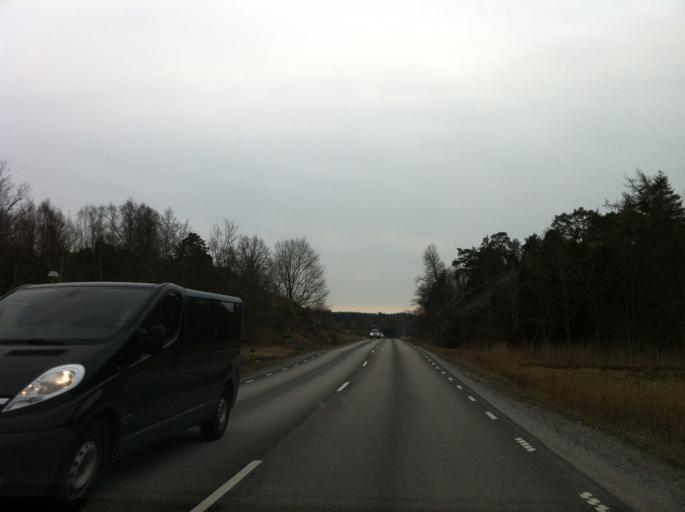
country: SE
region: Vaestra Goetaland
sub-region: Orust
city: Henan
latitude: 58.2311
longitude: 11.6831
